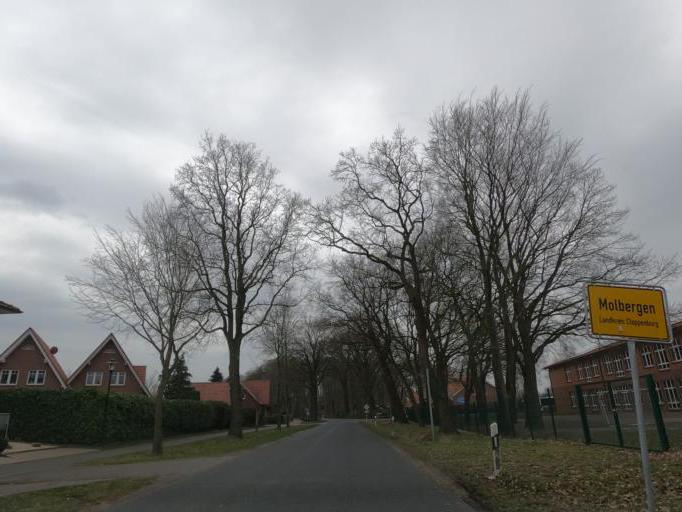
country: DE
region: Lower Saxony
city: Molbergen
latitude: 52.8638
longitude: 7.9240
